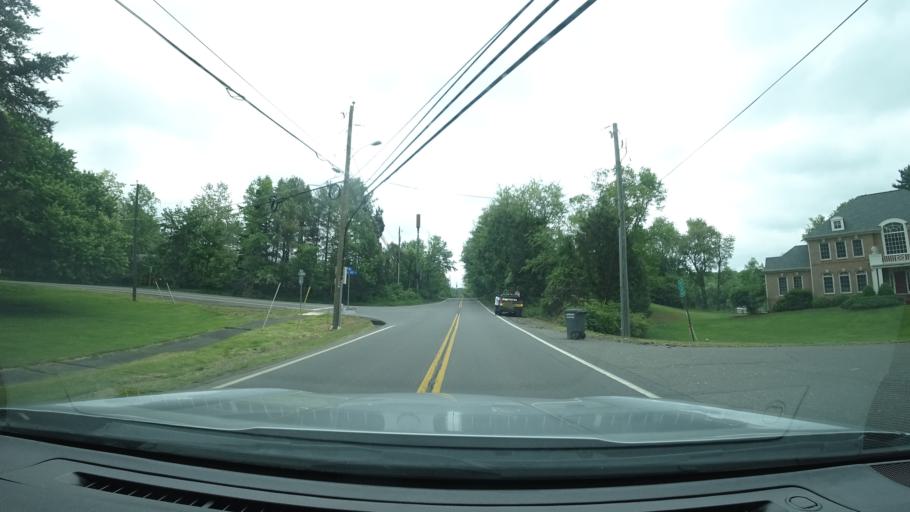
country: US
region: Virginia
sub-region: Fairfax County
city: Oak Hill
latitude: 38.9024
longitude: -77.3565
